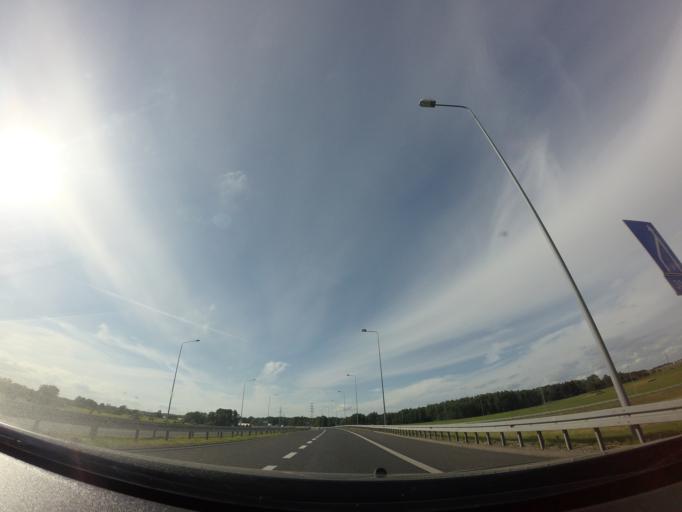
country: PL
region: West Pomeranian Voivodeship
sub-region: Powiat stargardzki
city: Kobylanka
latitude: 53.3493
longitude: 14.9492
